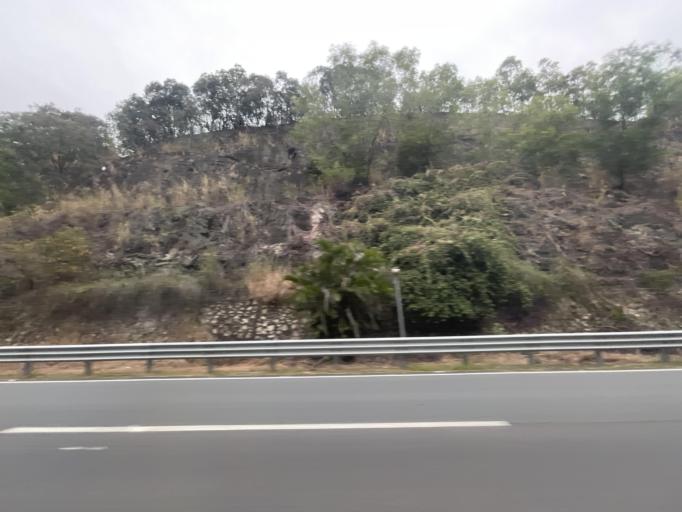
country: CN
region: Guangdong
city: Humen
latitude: 22.8074
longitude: 113.6428
